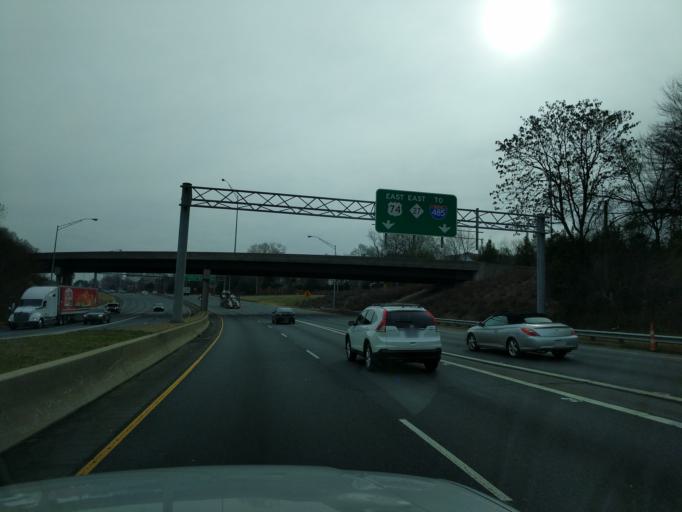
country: US
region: North Carolina
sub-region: Mecklenburg County
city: Charlotte
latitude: 35.2199
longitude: -80.8259
